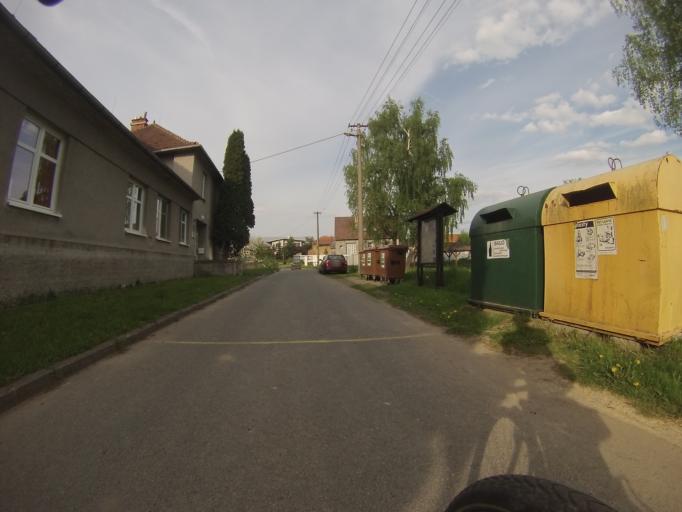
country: CZ
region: Olomoucky
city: Protivanov
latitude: 49.4415
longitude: 16.8553
